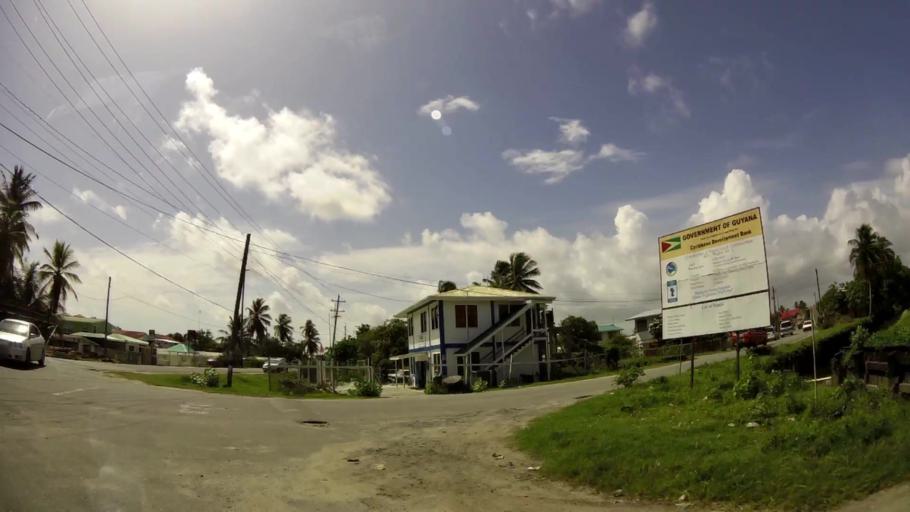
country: GY
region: Demerara-Mahaica
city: Mahaica Village
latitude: 6.7615
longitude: -57.9918
